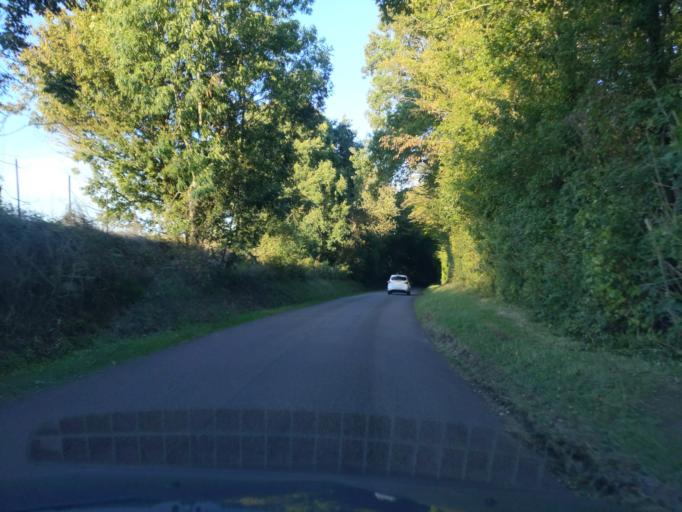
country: FR
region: Ile-de-France
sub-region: Departement de l'Essonne
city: Les Molieres
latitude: 48.6816
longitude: 2.0544
